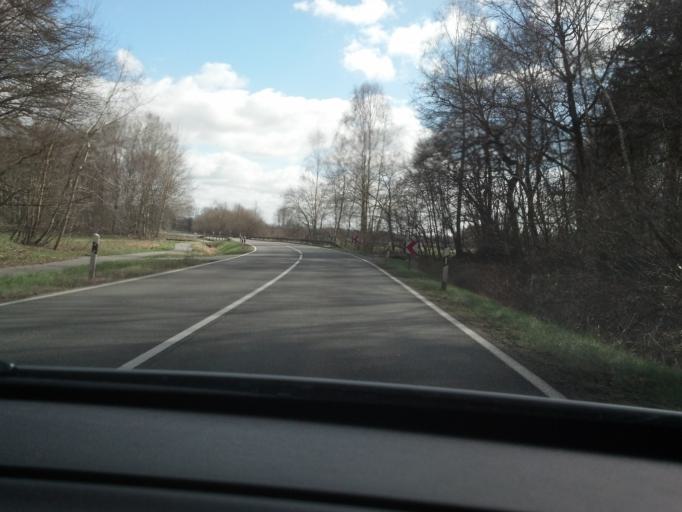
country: DE
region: Mecklenburg-Vorpommern
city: Zarrentin
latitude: 53.5027
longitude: 10.8717
